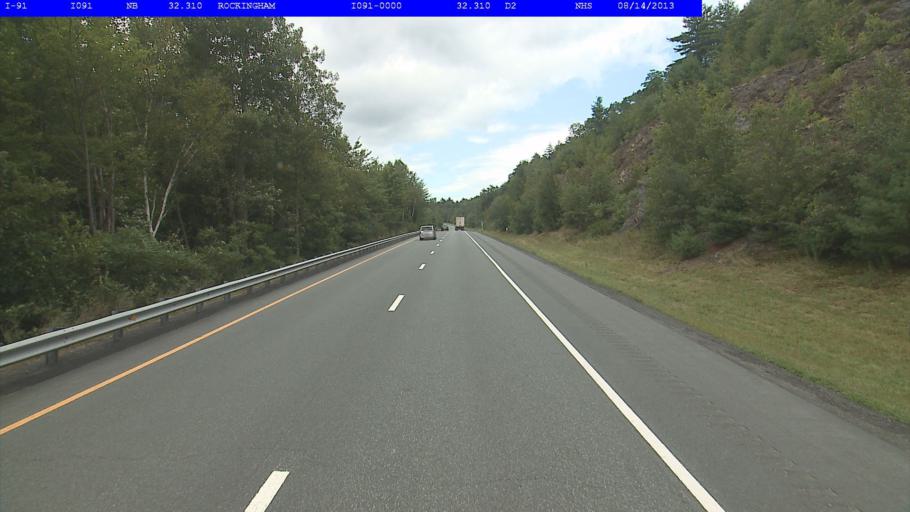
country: US
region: Vermont
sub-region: Windham County
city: Bellows Falls
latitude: 43.1399
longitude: -72.4755
